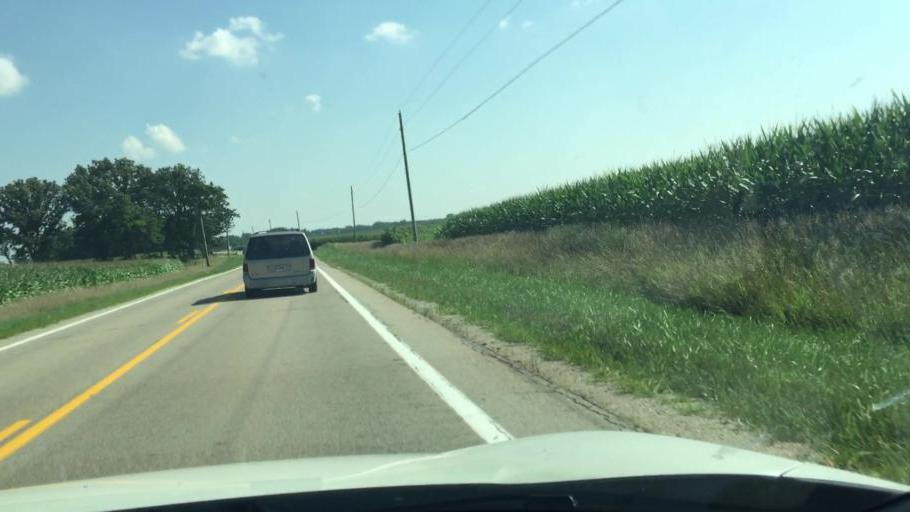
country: US
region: Ohio
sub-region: Champaign County
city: North Lewisburg
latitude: 40.1525
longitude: -83.5285
